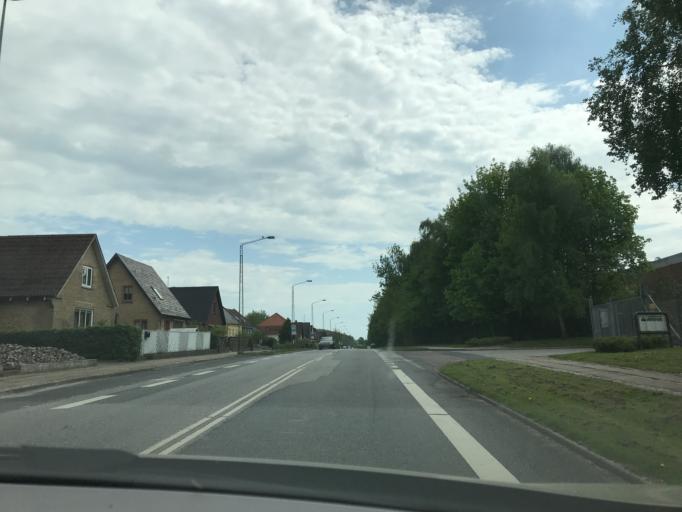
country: DK
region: South Denmark
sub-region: Assens Kommune
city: Assens
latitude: 55.2646
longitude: 9.9047
